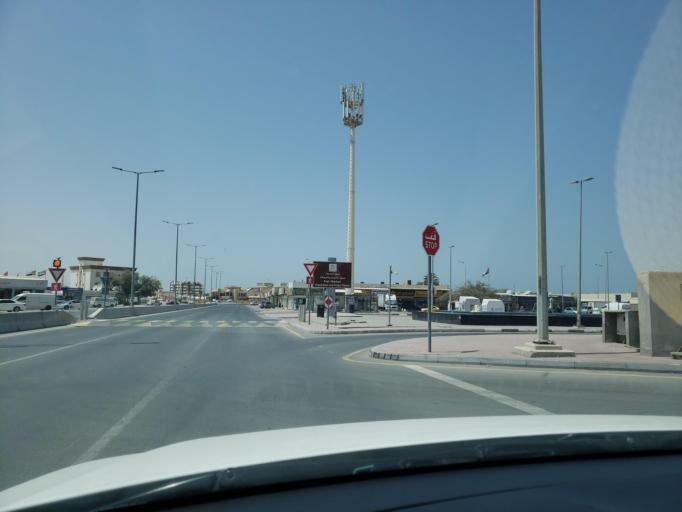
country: AE
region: Ra's al Khaymah
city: Ras al-Khaimah
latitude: 25.8166
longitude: 55.9695
